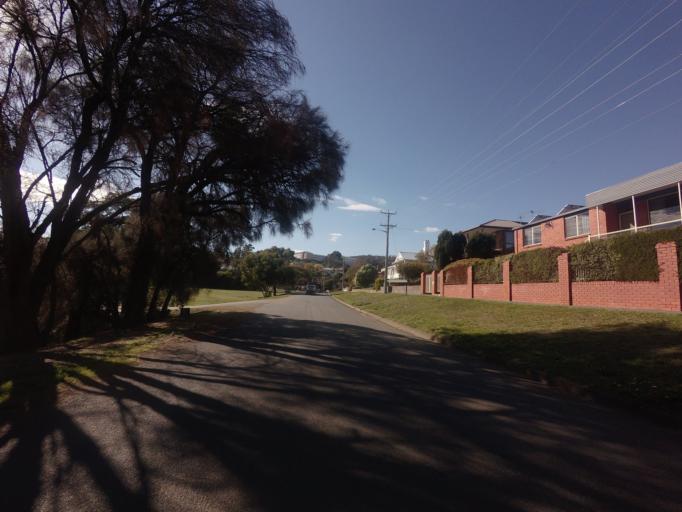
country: AU
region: Tasmania
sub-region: Clarence
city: Bellerive
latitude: -42.8657
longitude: 147.3555
